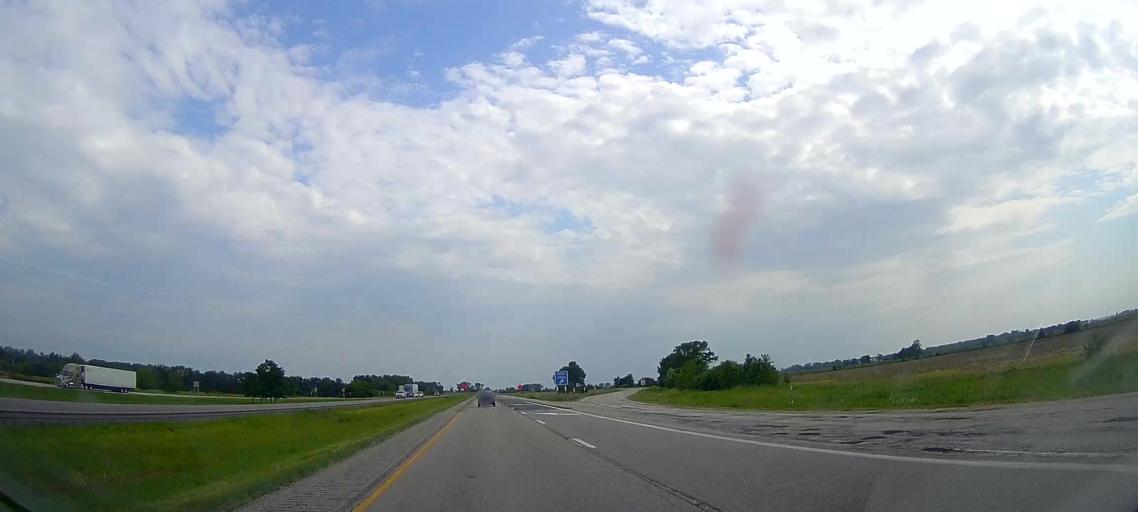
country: US
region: Nebraska
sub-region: Burt County
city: Tekamah
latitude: 41.7443
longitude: -96.0474
